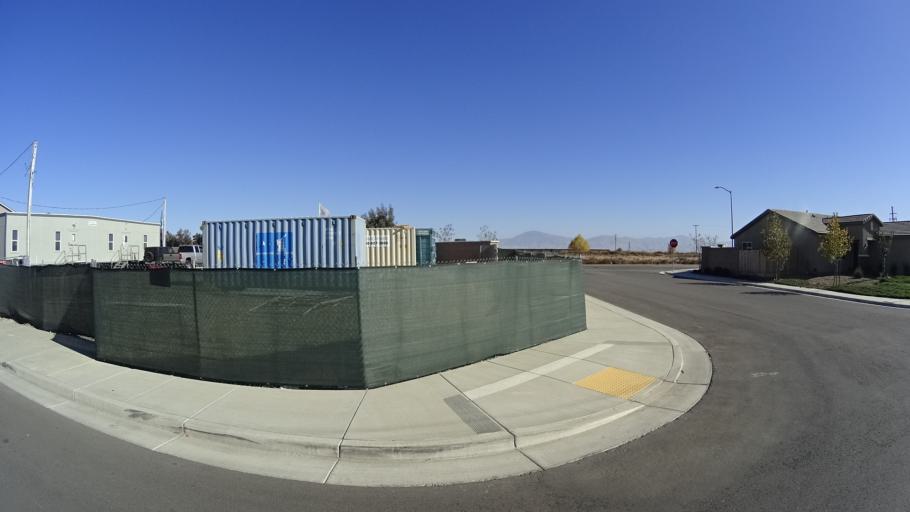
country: US
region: California
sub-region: Kern County
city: Greenfield
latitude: 35.2642
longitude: -119.0661
